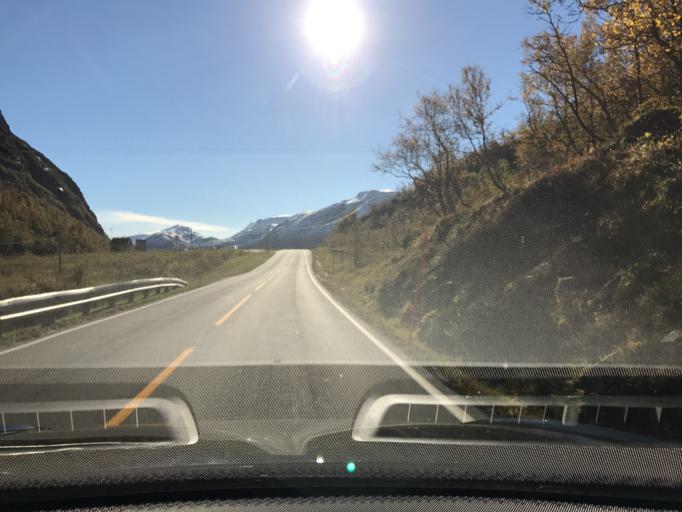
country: NO
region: More og Romsdal
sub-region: Norddal
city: Valldal
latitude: 62.1375
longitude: 7.1851
